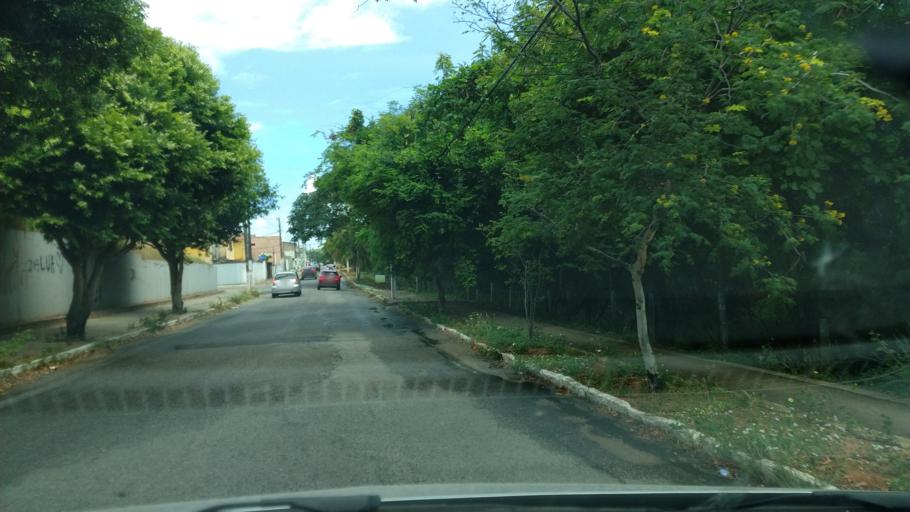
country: BR
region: Rio Grande do Norte
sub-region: Natal
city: Natal
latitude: -5.8537
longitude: -35.1998
